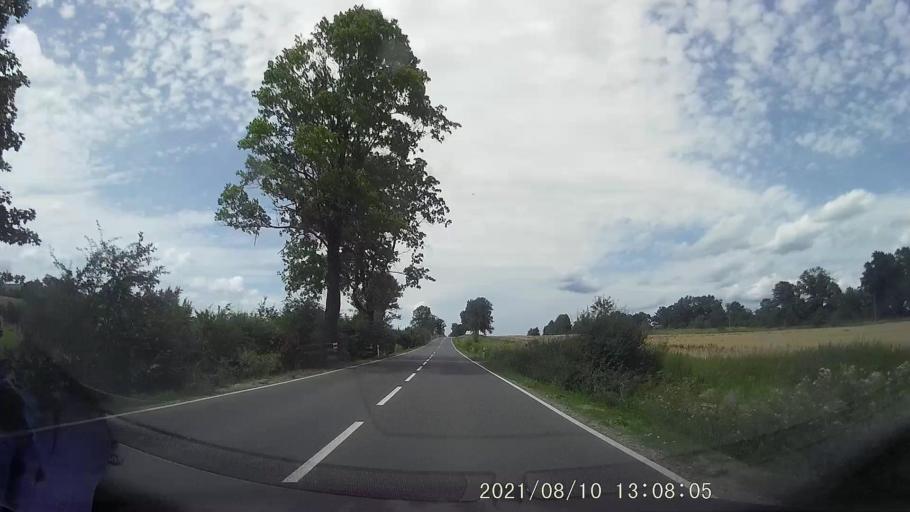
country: PL
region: Lower Silesian Voivodeship
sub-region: Powiat klodzki
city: Bozkow
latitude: 50.4908
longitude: 16.5636
